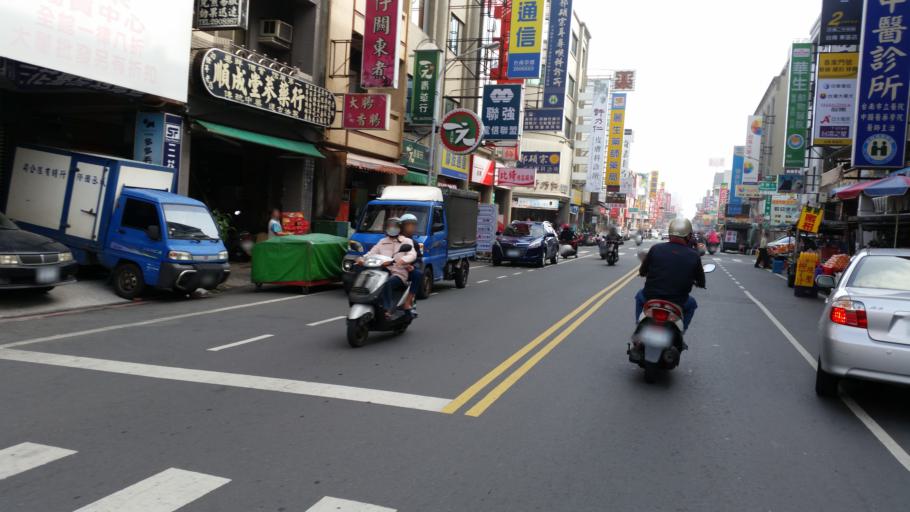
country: TW
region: Taiwan
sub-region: Tainan
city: Tainan
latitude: 22.9735
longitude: 120.2275
